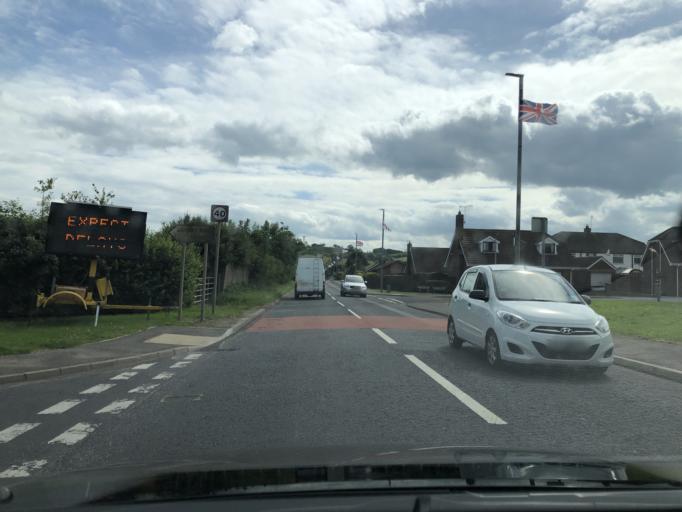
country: GB
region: Northern Ireland
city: Ballynahinch
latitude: 54.4117
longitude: -5.9038
